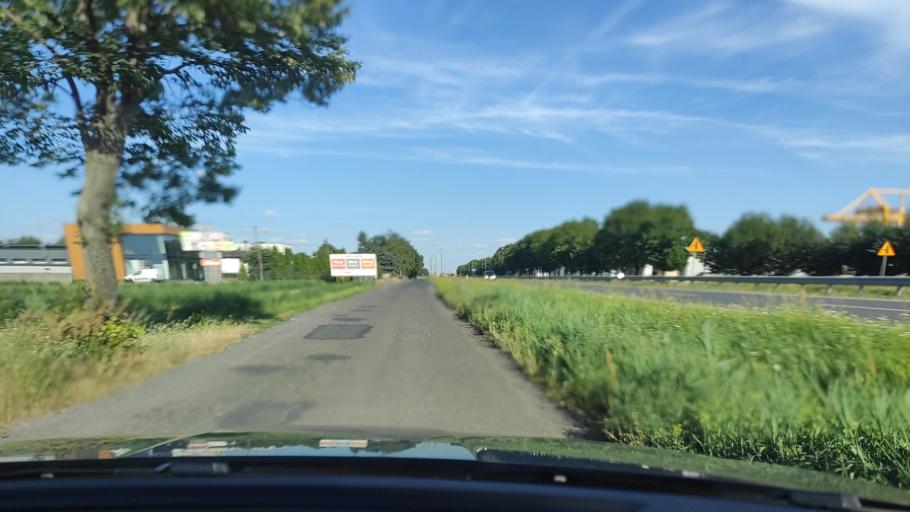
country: PL
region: Greater Poland Voivodeship
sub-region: Powiat poznanski
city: Swarzedz
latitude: 52.4007
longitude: 17.1333
